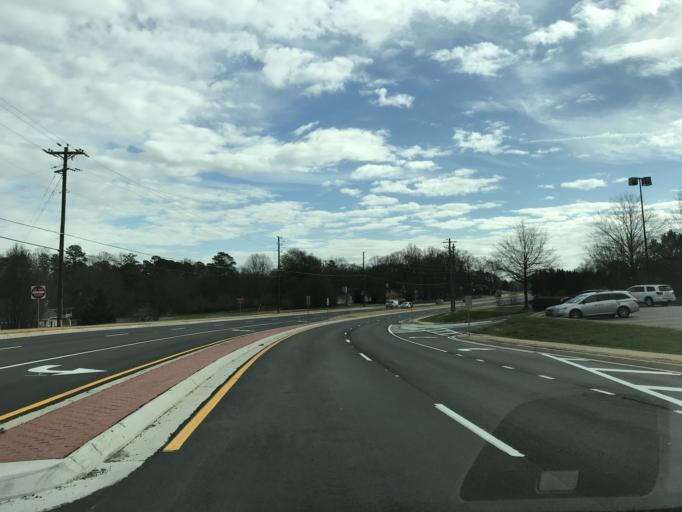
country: US
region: Georgia
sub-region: Forsyth County
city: Cumming
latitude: 34.1233
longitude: -84.1683
